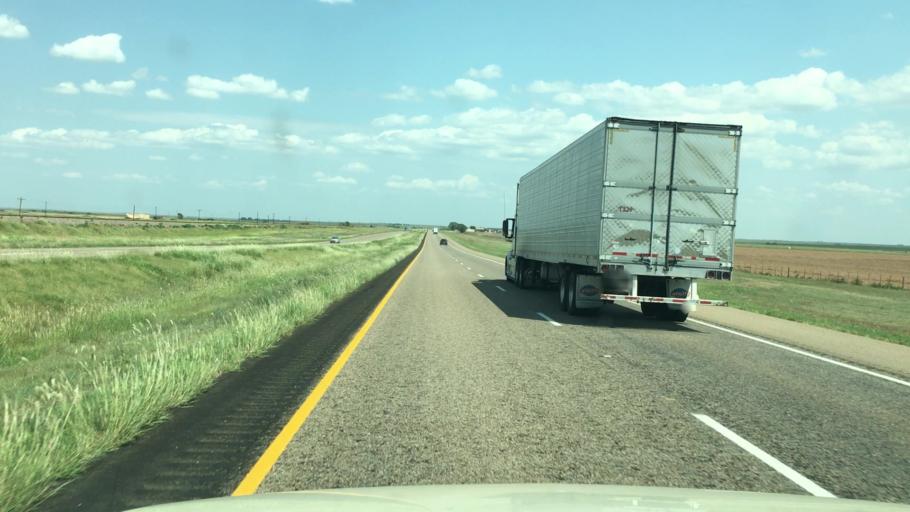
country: US
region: Texas
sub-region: Armstrong County
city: Claude
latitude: 35.0320
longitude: -101.1317
